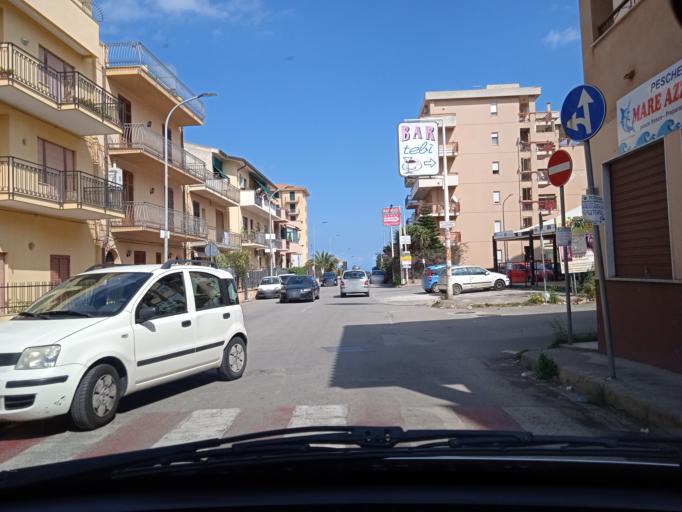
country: IT
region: Sicily
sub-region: Palermo
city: Casteldaccia
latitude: 38.0551
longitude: 13.5332
